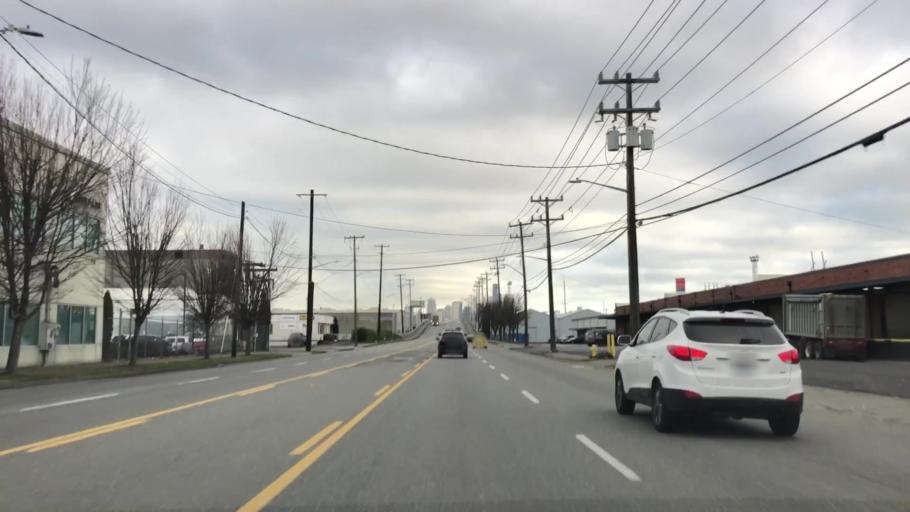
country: US
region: Washington
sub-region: King County
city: White Center
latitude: 47.5580
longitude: -122.3342
